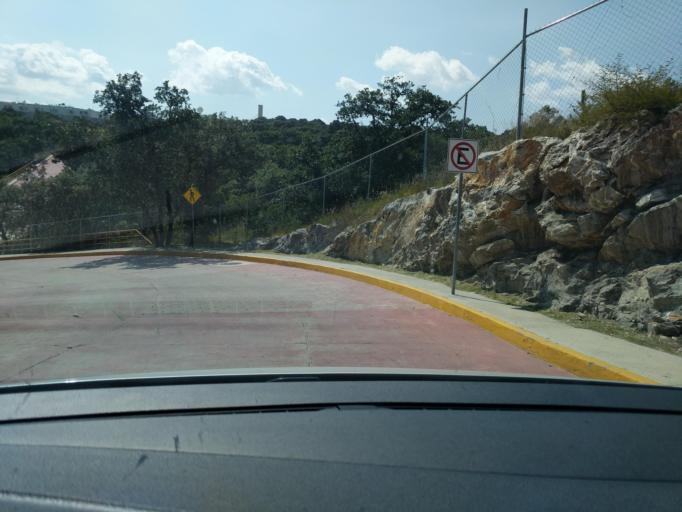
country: MX
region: Puebla
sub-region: Puebla
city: Galaxia la Calera
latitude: 19.0074
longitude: -98.1454
